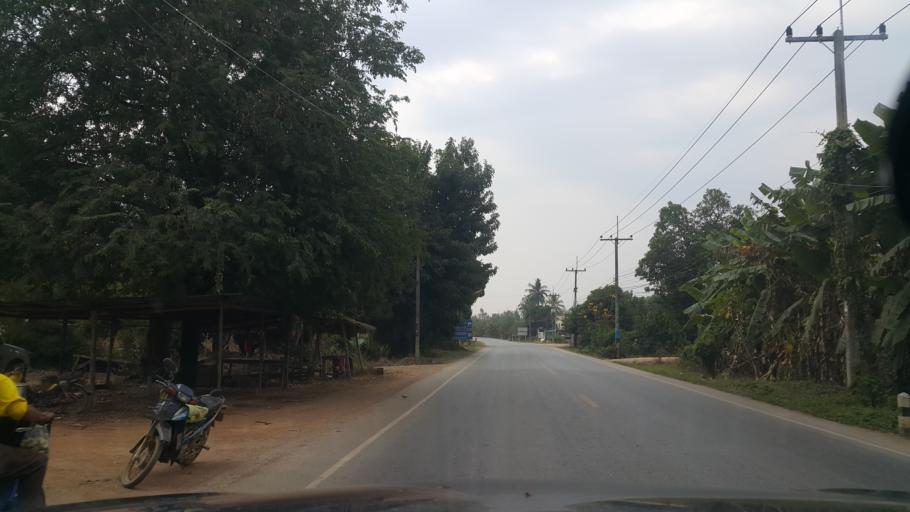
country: TH
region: Sukhothai
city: Si Samrong
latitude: 17.0833
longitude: 99.8815
